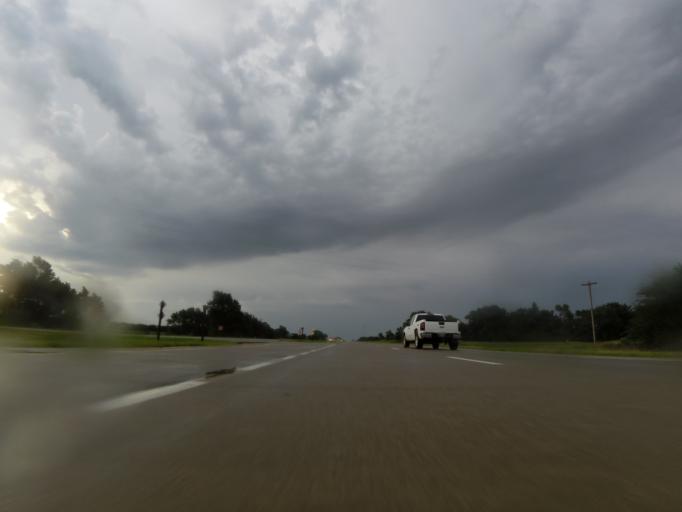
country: US
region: Kansas
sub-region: Reno County
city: Haven
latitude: 37.9205
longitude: -97.8306
